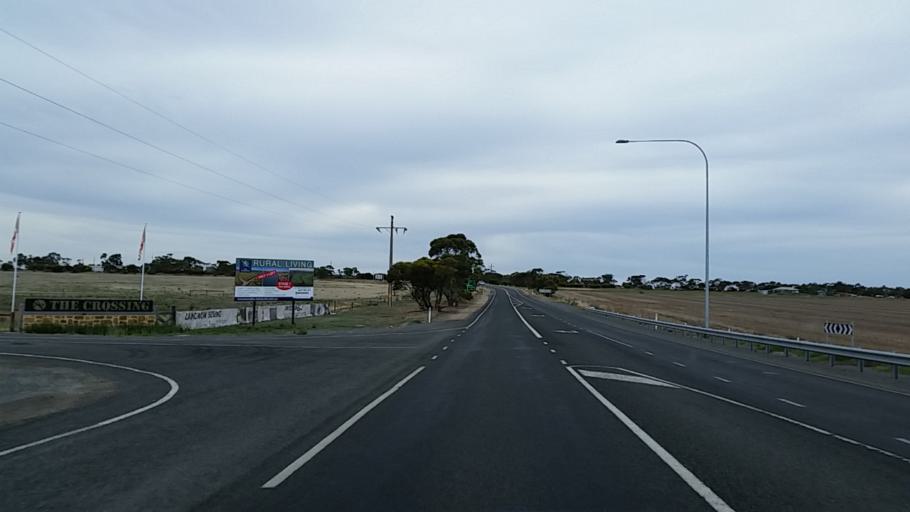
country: AU
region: South Australia
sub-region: Mid Murray
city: Mannum
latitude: -34.9070
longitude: 139.2783
